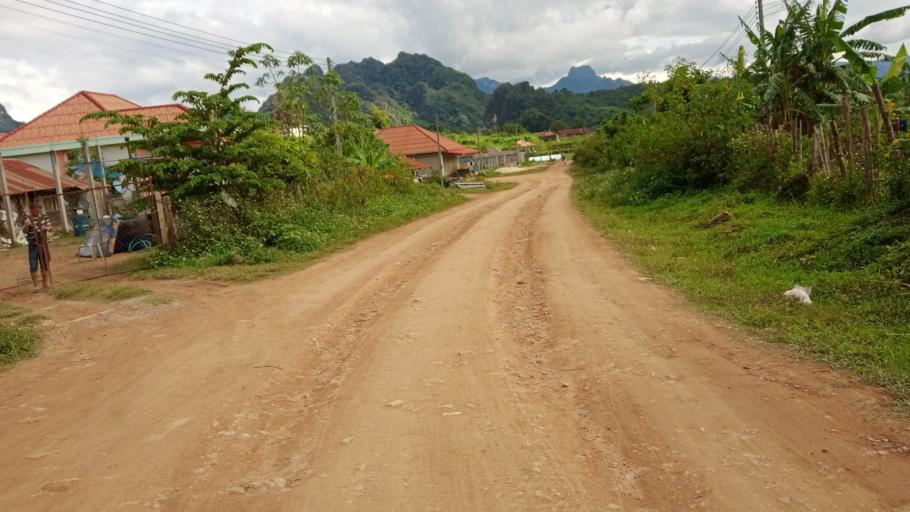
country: LA
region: Xiangkhoang
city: Phonsavan
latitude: 19.1082
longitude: 102.9267
